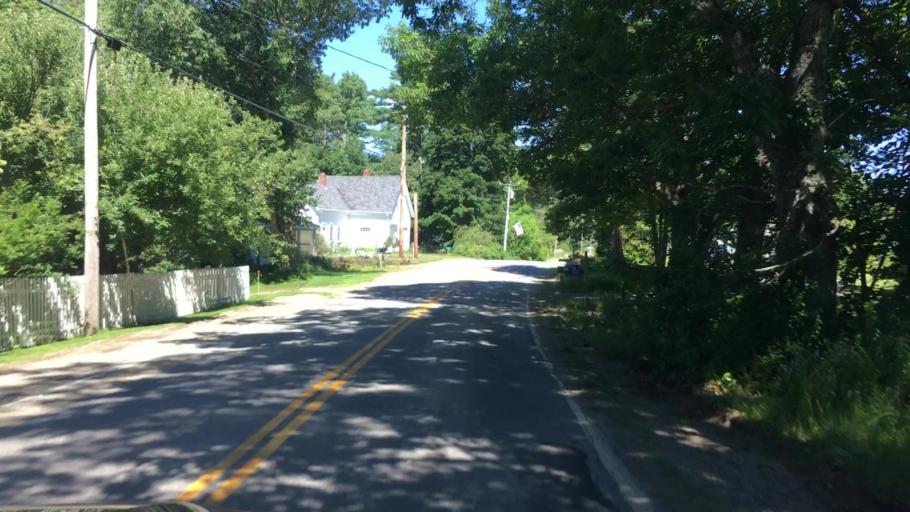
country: US
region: Maine
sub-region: Hancock County
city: Penobscot
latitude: 44.4561
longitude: -68.7035
